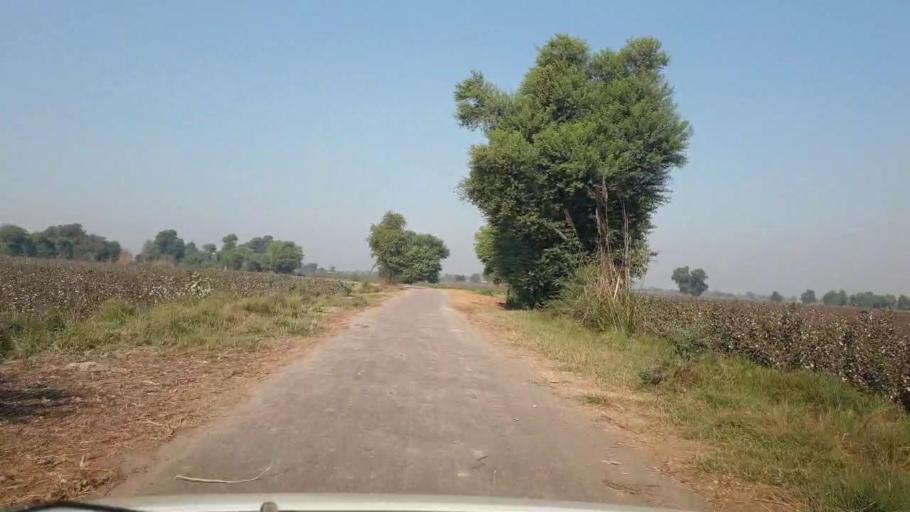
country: PK
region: Sindh
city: Bhan
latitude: 26.6030
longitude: 67.7513
